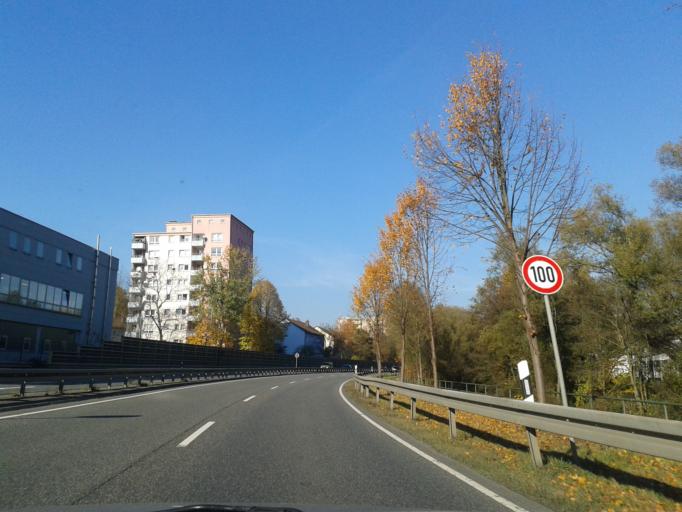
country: DE
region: Hesse
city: Dillenburg
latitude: 50.7245
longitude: 8.2935
